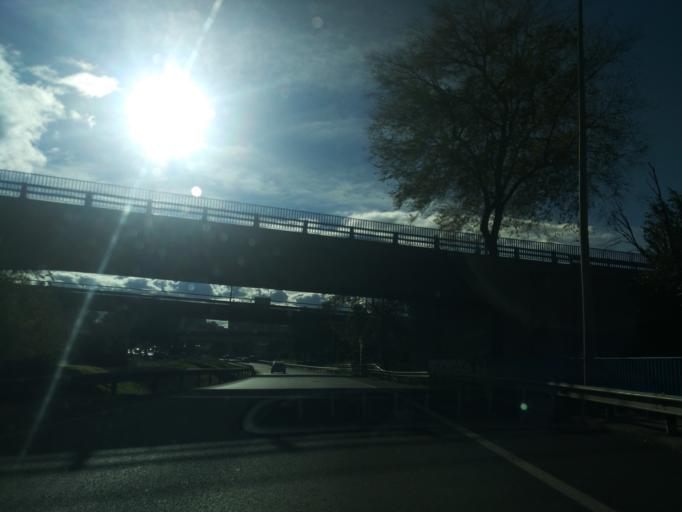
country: ES
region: Madrid
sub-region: Provincia de Madrid
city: Usera
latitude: 40.3824
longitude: -3.6898
